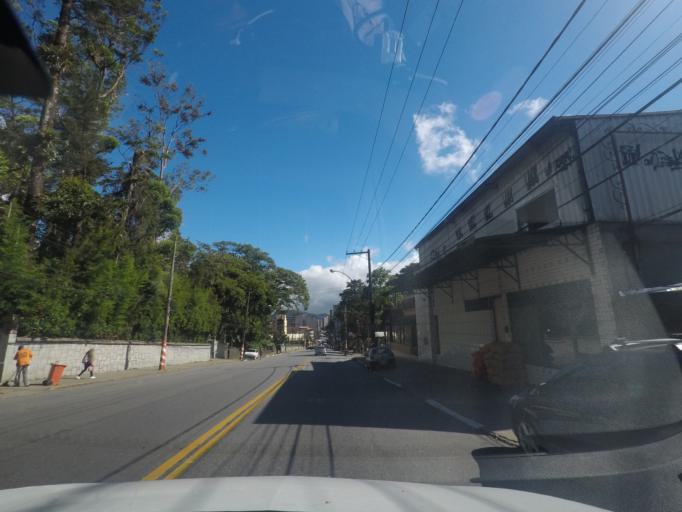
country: BR
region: Rio de Janeiro
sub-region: Teresopolis
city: Teresopolis
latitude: -22.4430
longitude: -42.9809
